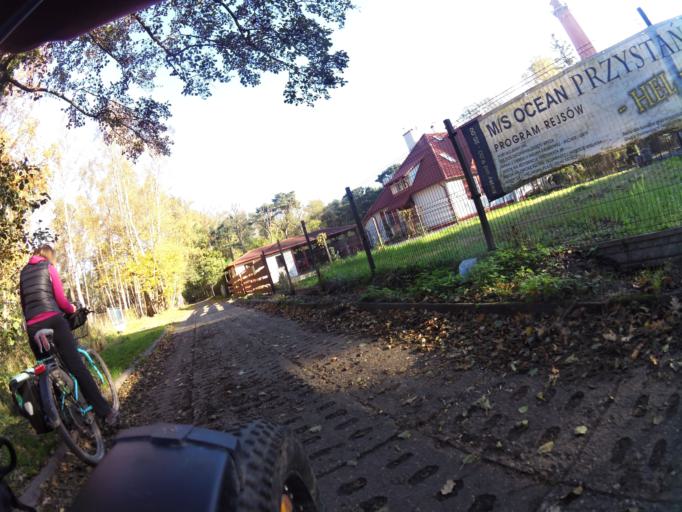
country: PL
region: Pomeranian Voivodeship
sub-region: Powiat pucki
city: Hel
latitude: 54.6003
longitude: 18.8118
